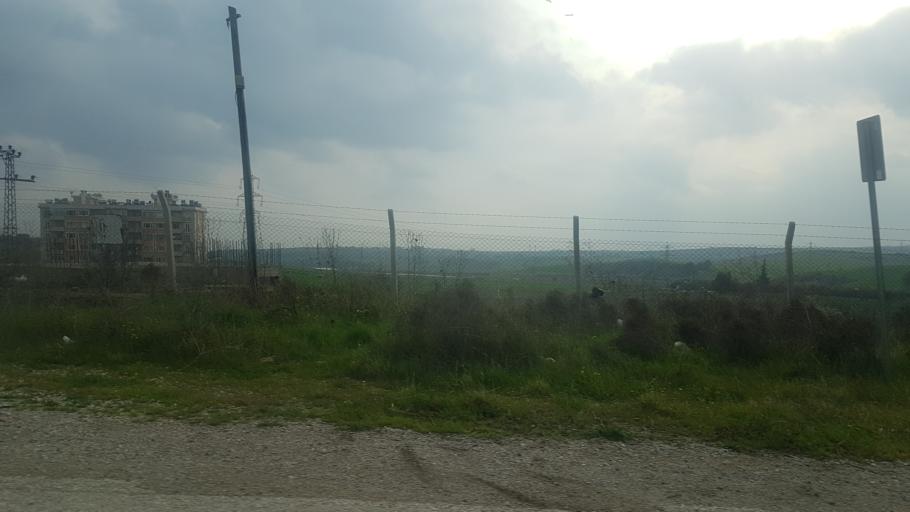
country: TR
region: Mersin
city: Yenice
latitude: 37.0522
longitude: 35.1726
